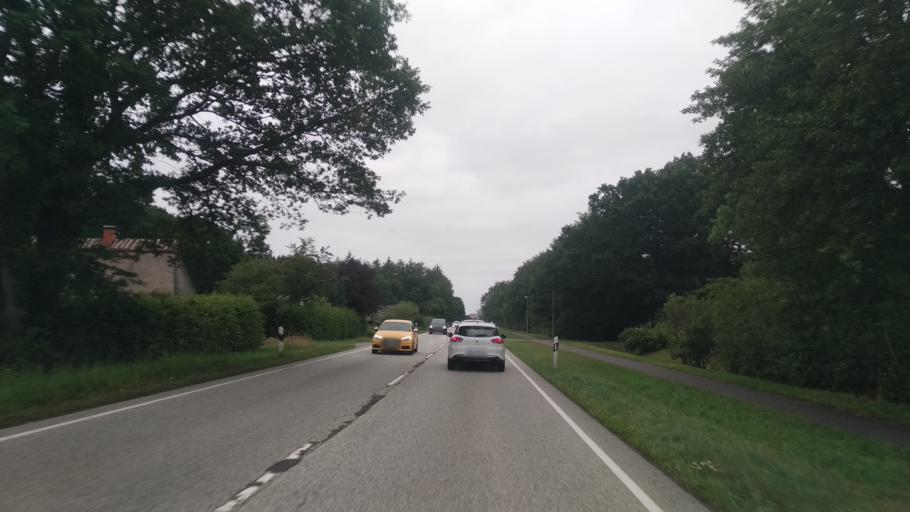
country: DE
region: Schleswig-Holstein
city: Oeversee
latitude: 54.6964
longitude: 9.4334
